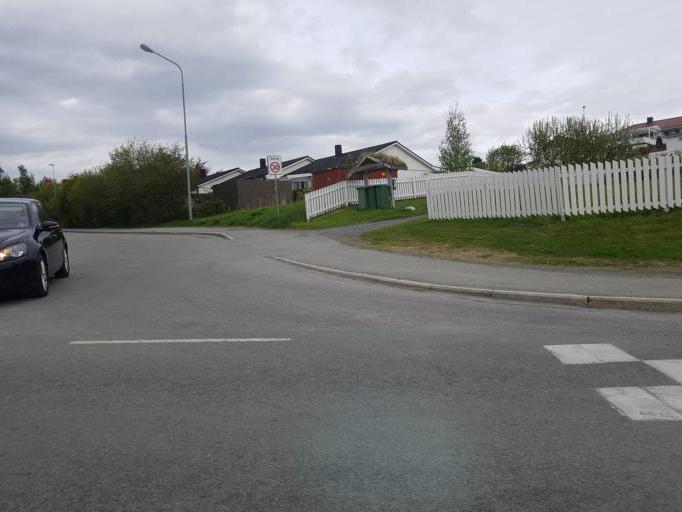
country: NO
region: Nord-Trondelag
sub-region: Levanger
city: Levanger
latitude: 63.7489
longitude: 11.2747
